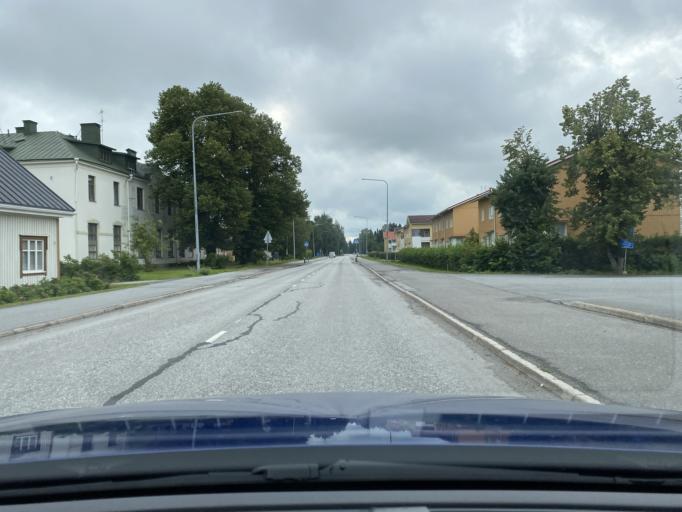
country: FI
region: Ostrobothnia
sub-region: Kyroenmaa
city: Laihia
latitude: 62.9755
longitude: 22.0137
